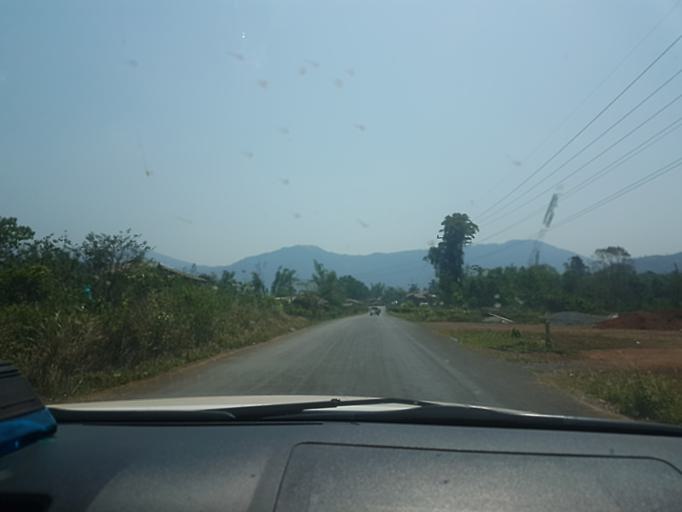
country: LA
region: Bolikhamxai
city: Ban Nahin
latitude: 18.5332
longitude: 104.4783
